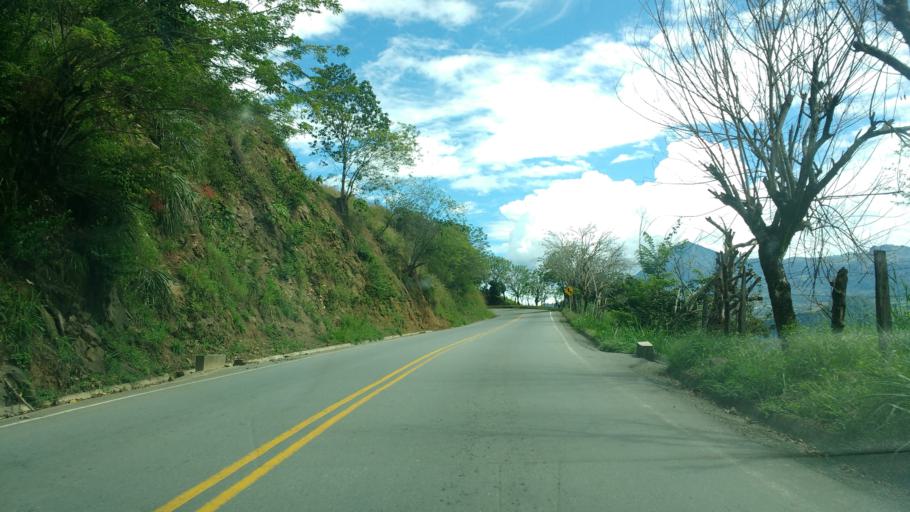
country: CO
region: Antioquia
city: Titiribi
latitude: 6.0244
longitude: -75.7680
